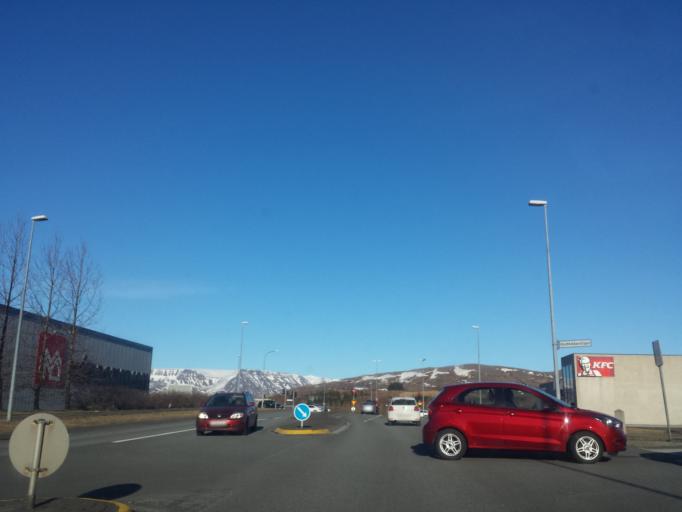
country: IS
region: Capital Region
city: Mosfellsbaer
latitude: 64.1305
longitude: -21.7617
